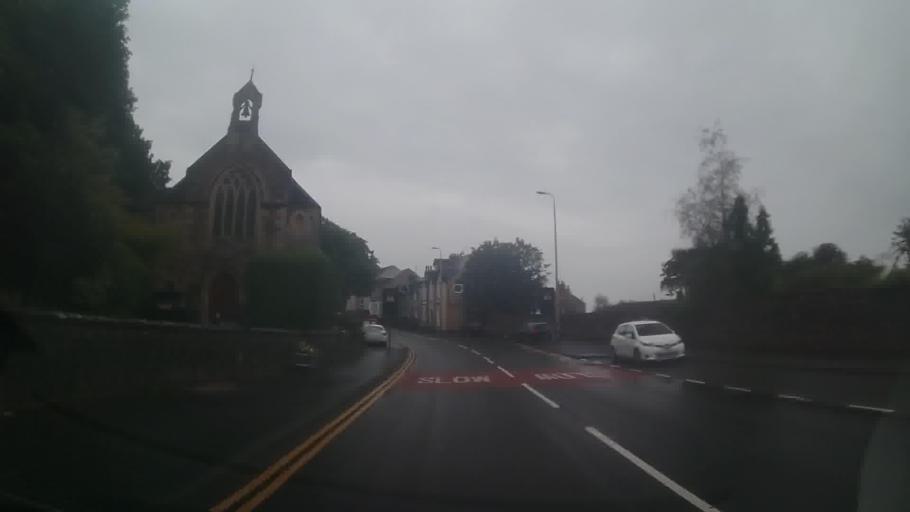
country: GB
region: Scotland
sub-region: North Ayrshire
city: Fairlie
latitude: 55.7576
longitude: -4.8543
